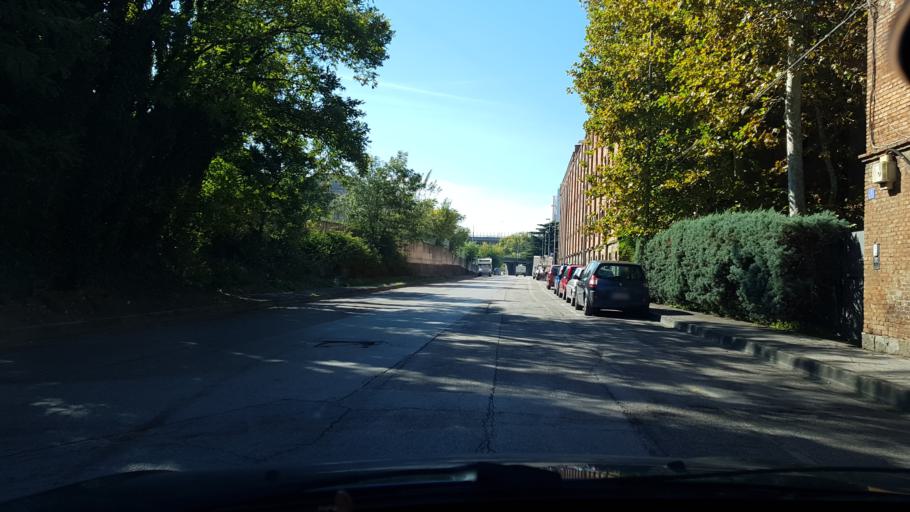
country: IT
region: Friuli Venezia Giulia
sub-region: Provincia di Trieste
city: Trieste
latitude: 45.6210
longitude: 13.7900
